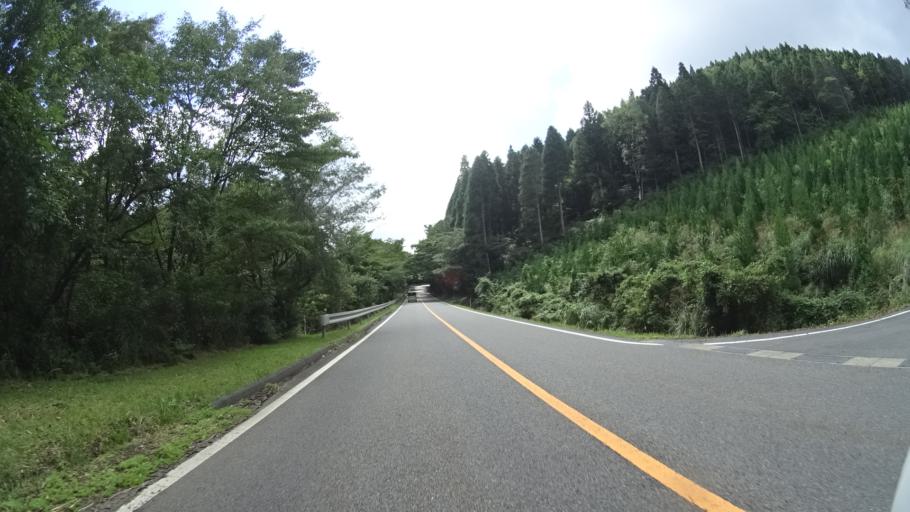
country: JP
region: Oita
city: Tsukawaki
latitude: 33.2006
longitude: 131.2869
